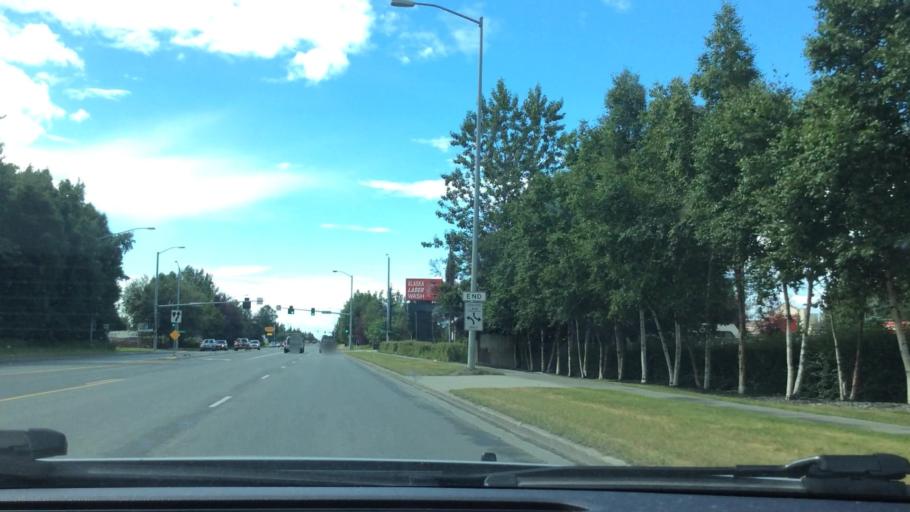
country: US
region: Alaska
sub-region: Anchorage Municipality
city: Anchorage
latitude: 61.2098
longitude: -149.7978
